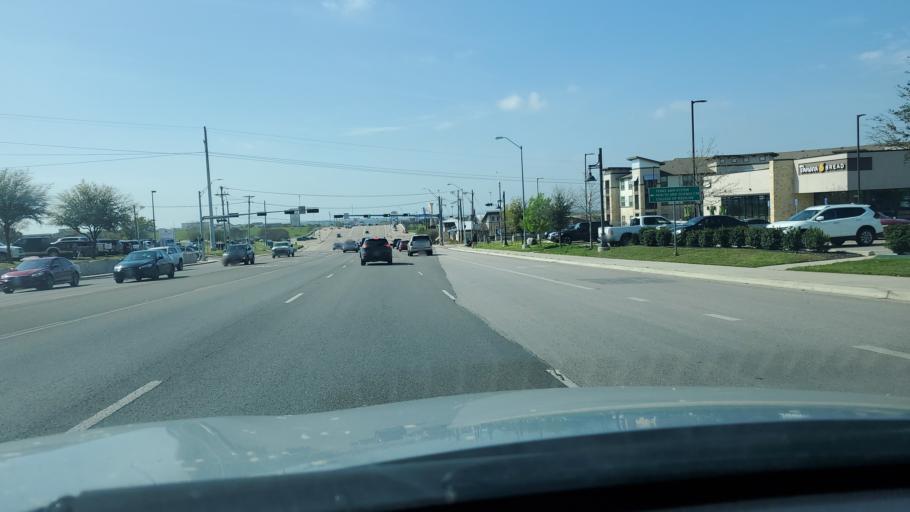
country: US
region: Texas
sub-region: Bell County
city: Temple
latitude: 31.0773
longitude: -97.3666
